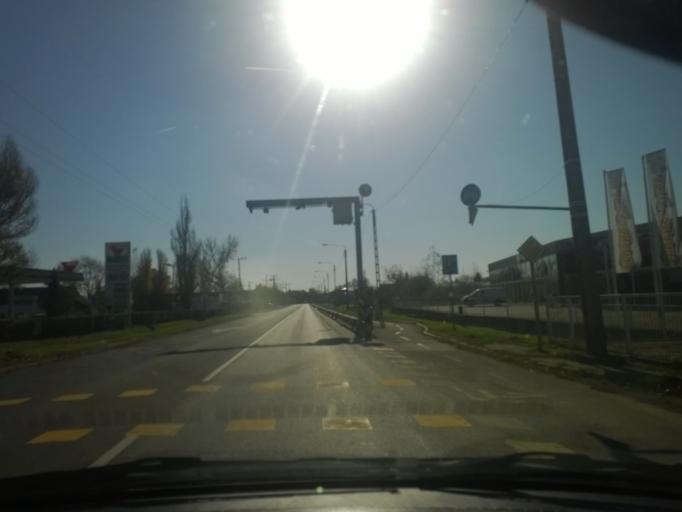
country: HU
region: Csongrad
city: Hodmezovasarhely
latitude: 46.4347
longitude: 20.3183
